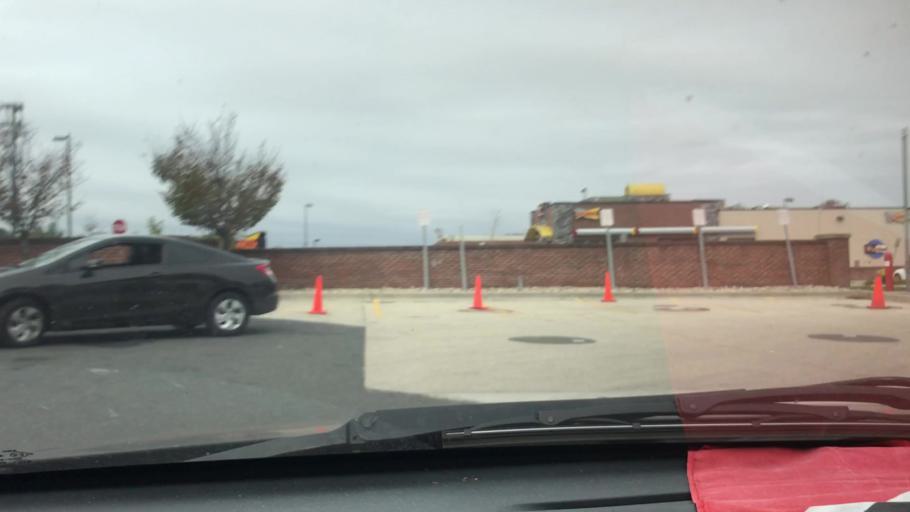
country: US
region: Maryland
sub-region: Prince George's County
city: Forestville
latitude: 38.8701
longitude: -76.8512
